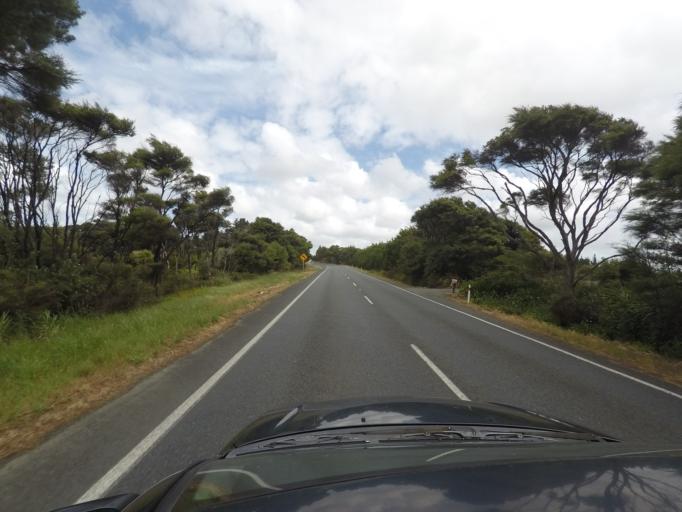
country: NZ
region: Auckland
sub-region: Auckland
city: Parakai
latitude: -36.5688
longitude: 174.4761
